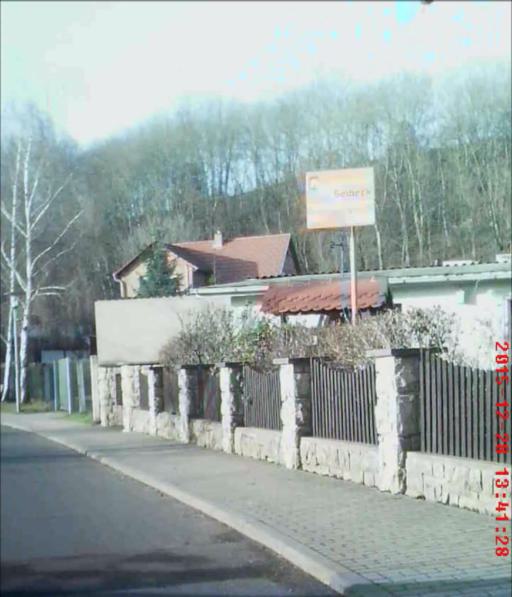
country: DE
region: Thuringia
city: Eberstedt
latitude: 51.0756
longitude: 11.5835
